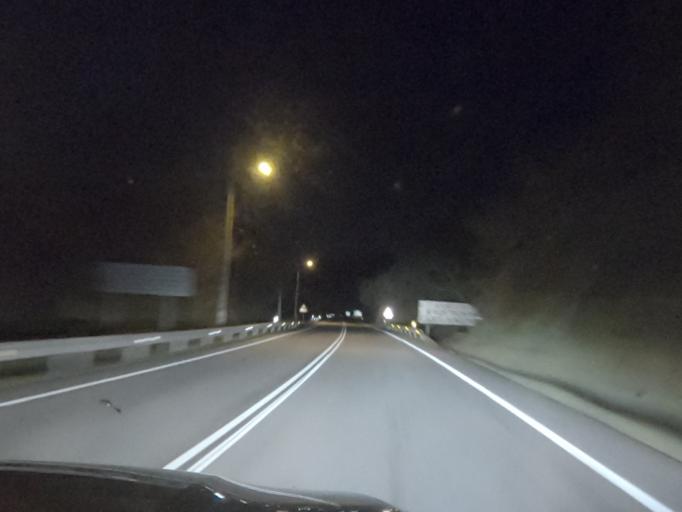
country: ES
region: Galicia
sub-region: Provincia de Ourense
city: Cualedro
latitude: 41.9685
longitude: -7.5195
